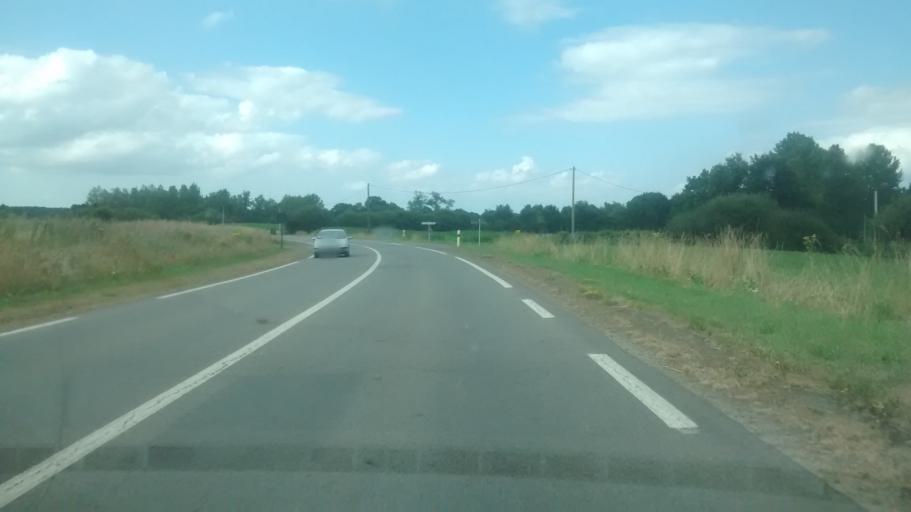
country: FR
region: Brittany
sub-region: Departement d'Ille-et-Vilaine
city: Saint-Meen-le-Grand
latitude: 48.1936
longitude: -2.1701
